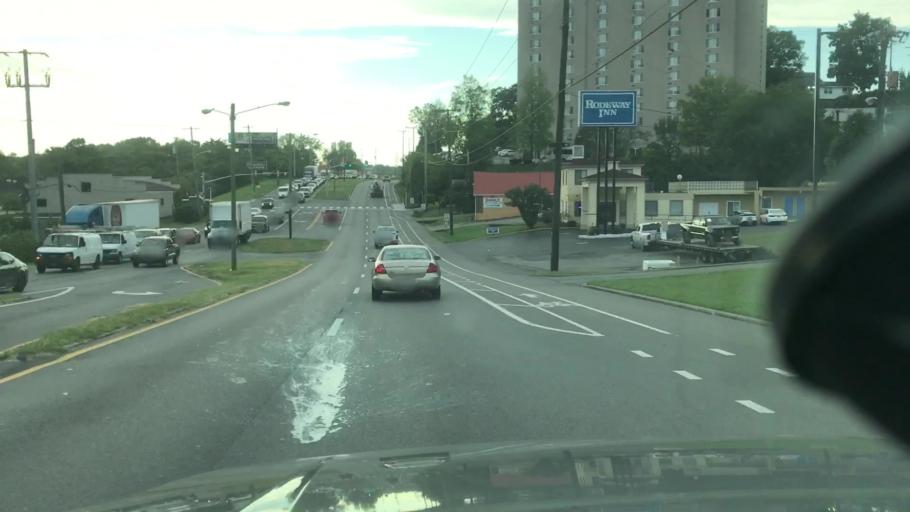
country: US
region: Tennessee
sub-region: Davidson County
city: Nashville
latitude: 36.1330
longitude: -86.7209
